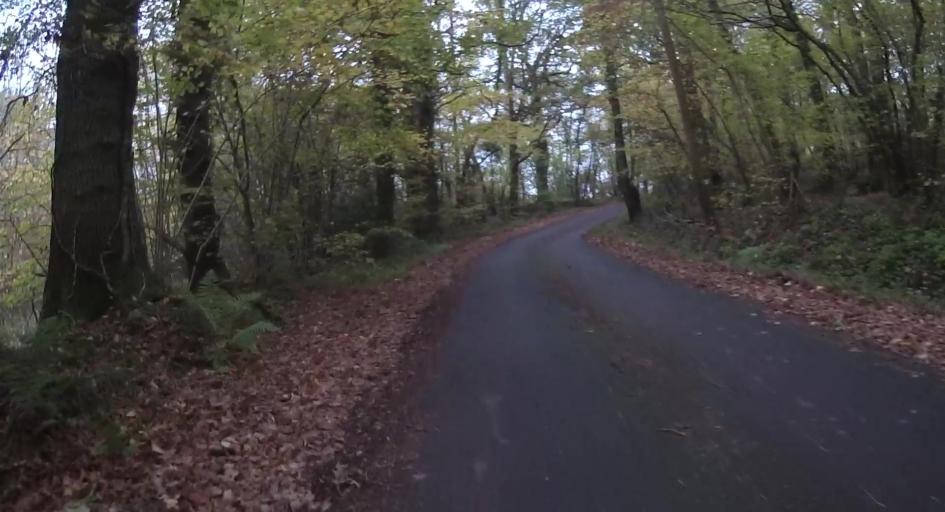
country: GB
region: England
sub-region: Surrey
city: Farnham
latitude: 51.1696
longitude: -0.8235
